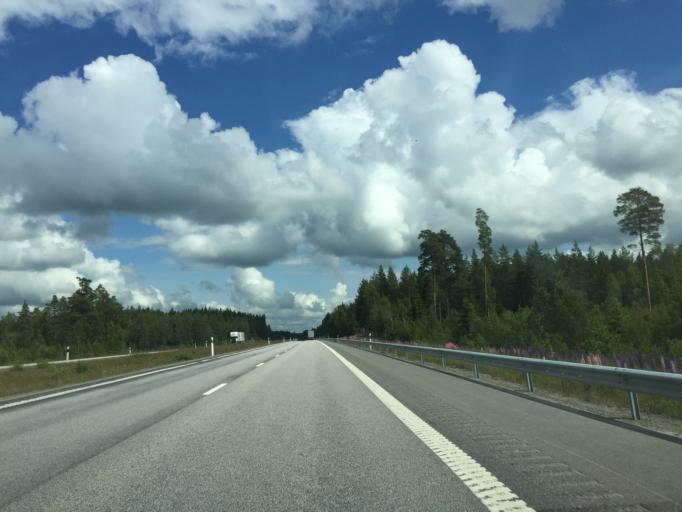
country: SE
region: OErebro
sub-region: Lindesbergs Kommun
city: Fellingsbro
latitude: 59.3527
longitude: 15.5605
